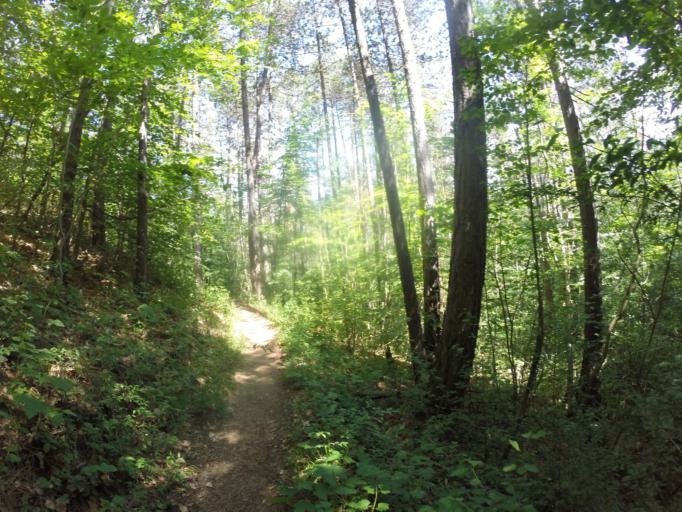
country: DE
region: Thuringia
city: Zollnitz
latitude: 50.8975
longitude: 11.6402
